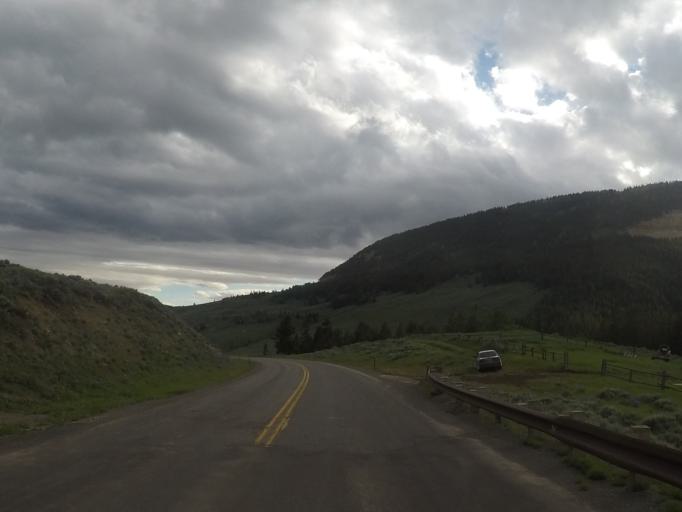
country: US
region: Wyoming
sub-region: Big Horn County
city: Greybull
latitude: 44.6043
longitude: -107.5303
